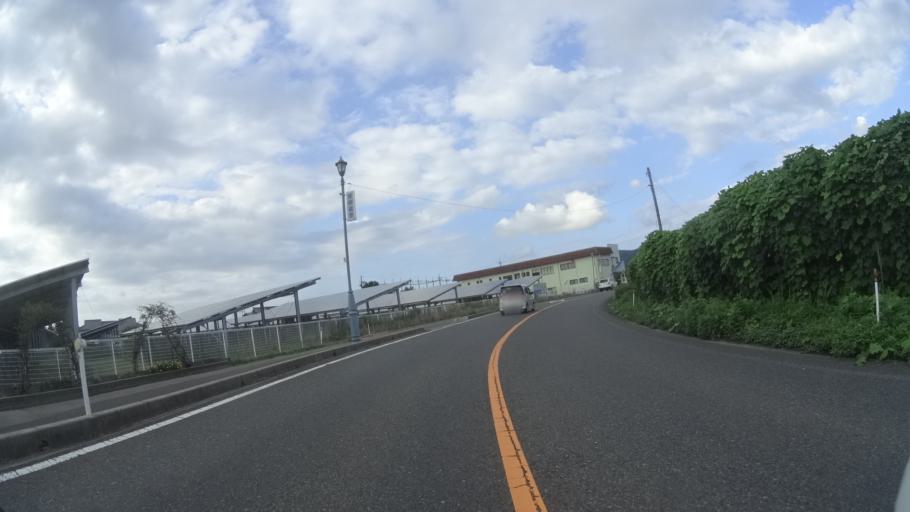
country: JP
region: Tottori
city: Kurayoshi
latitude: 35.4666
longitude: 133.8945
